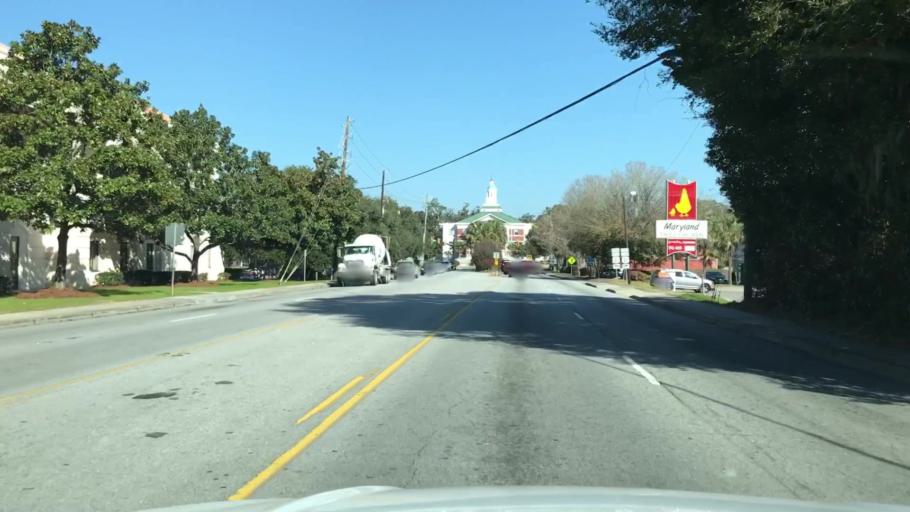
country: US
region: South Carolina
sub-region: Beaufort County
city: Beaufort
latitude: 32.4383
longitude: -80.6858
